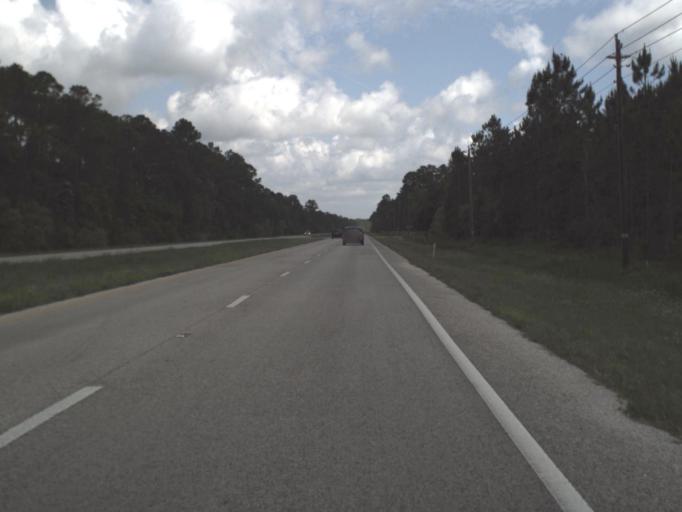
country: US
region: Florida
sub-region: Saint Johns County
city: Butler Beach
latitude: 29.7373
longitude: -81.3078
